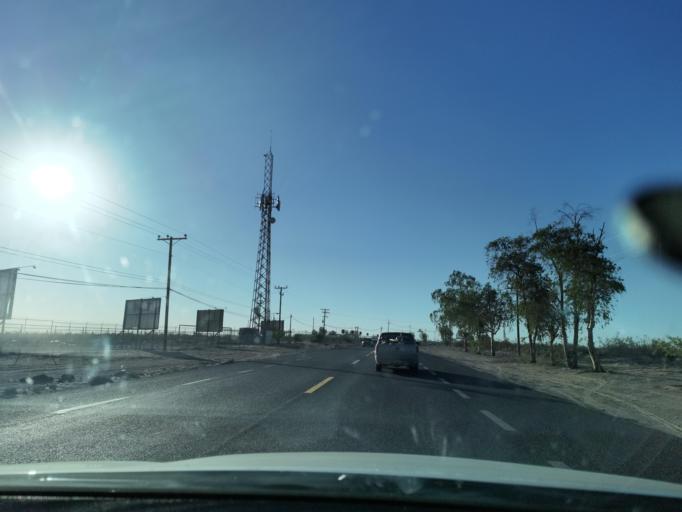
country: MX
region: Baja California
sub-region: Mexicali
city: Islas Agrarias Grupo A
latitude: 32.6302
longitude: -115.2579
